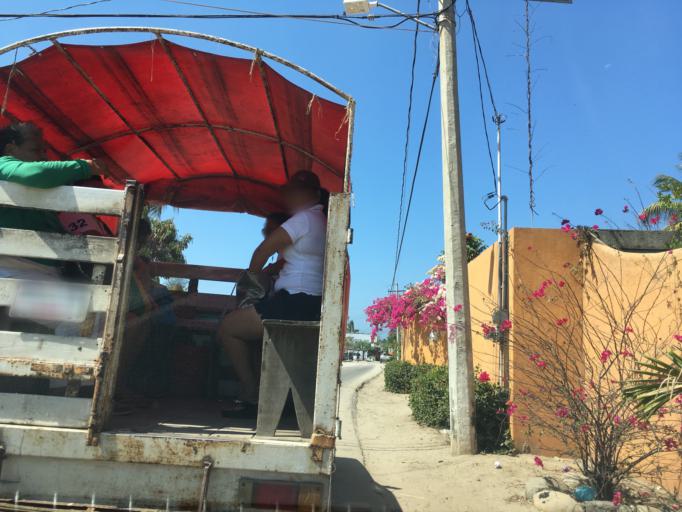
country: MX
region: Guerrero
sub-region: Zihuatanejo de Azueta
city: Los Achotes
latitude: 17.5384
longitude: -101.4412
